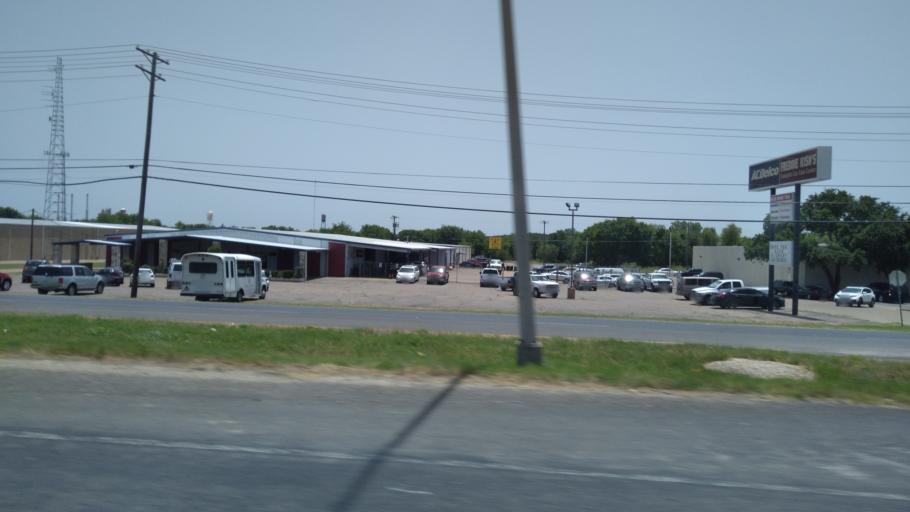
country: US
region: Texas
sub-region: McLennan County
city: Beverly Hills
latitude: 31.5174
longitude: -97.1794
